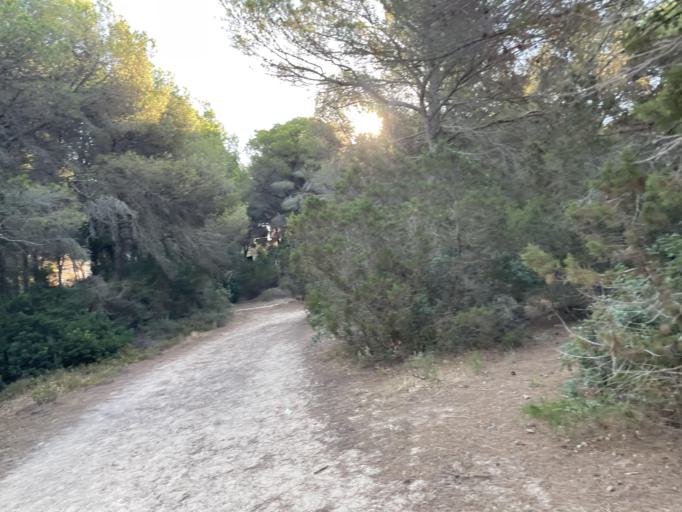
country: ES
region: Balearic Islands
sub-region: Illes Balears
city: Capdepera
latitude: 39.7169
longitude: 3.4551
